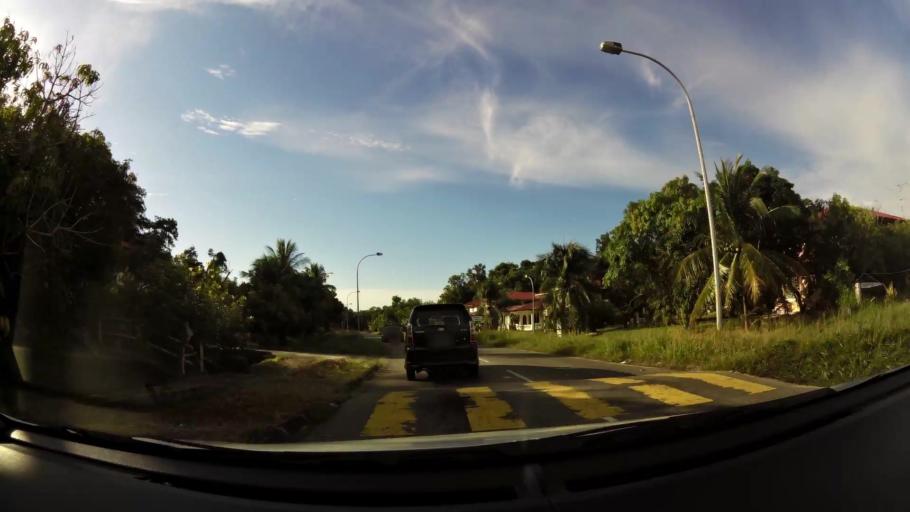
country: BN
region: Brunei and Muara
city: Bandar Seri Begawan
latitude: 4.9825
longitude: 114.9649
